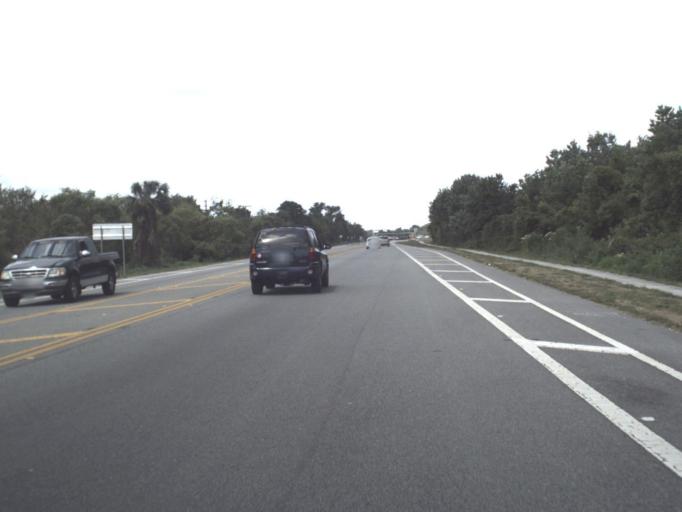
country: US
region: Florida
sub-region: Brevard County
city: Cocoa
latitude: 28.3971
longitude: -80.7568
